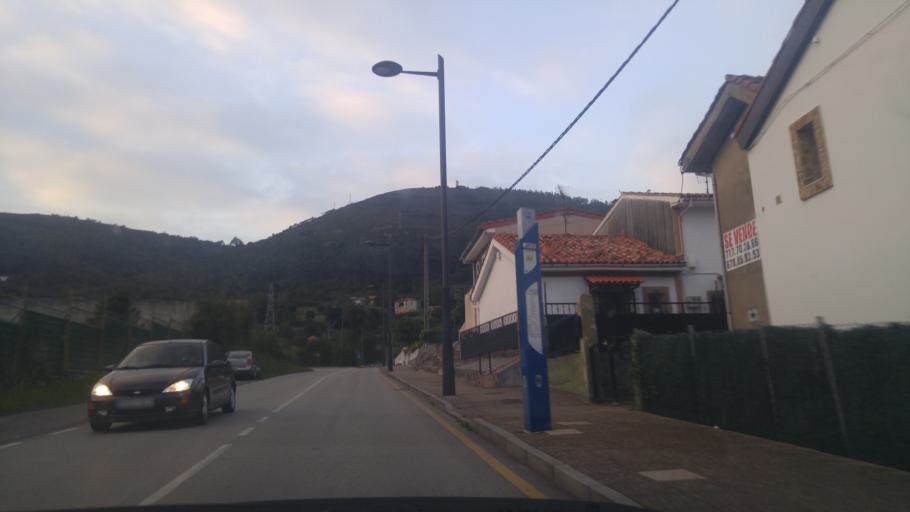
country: ES
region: Asturias
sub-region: Province of Asturias
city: Oviedo
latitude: 43.3751
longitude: -5.8644
